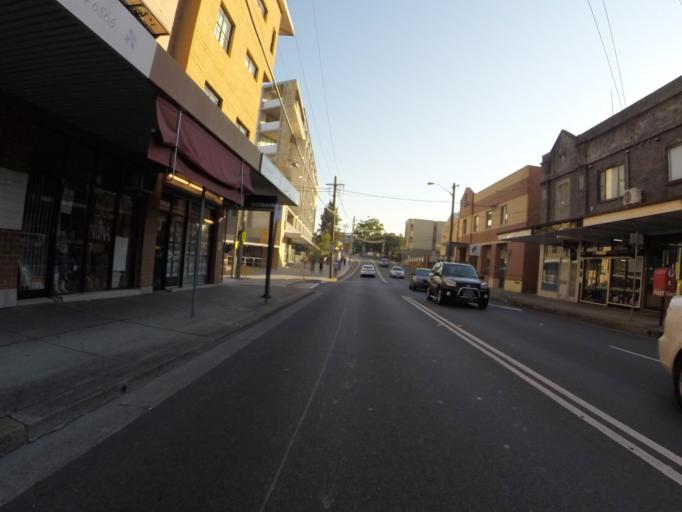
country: AU
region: New South Wales
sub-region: Marrickville
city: Marrickville
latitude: -33.9127
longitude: 151.1541
